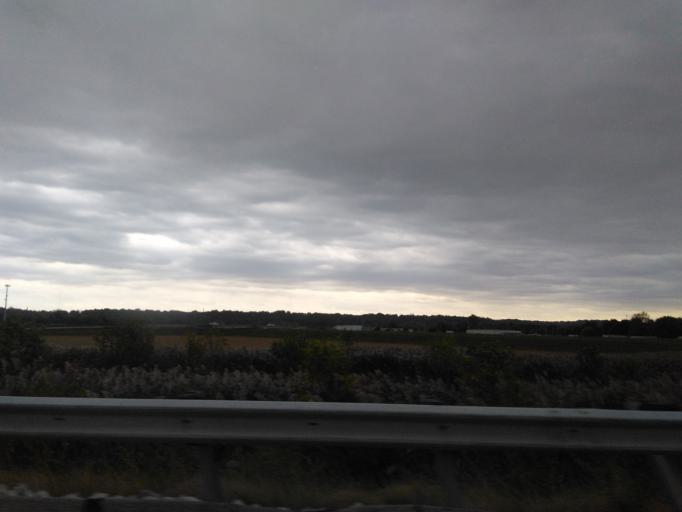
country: US
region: Illinois
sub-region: Saint Clair County
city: Caseyville
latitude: 38.6420
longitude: -90.0495
